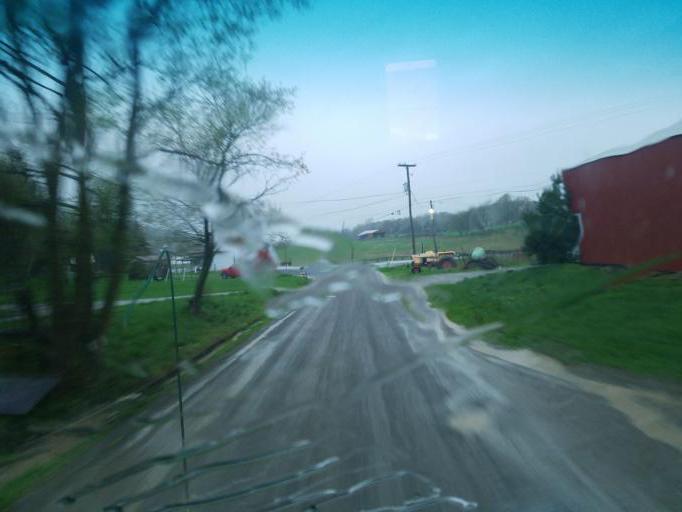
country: US
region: Pennsylvania
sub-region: Tioga County
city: Westfield
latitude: 41.9204
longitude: -77.7440
